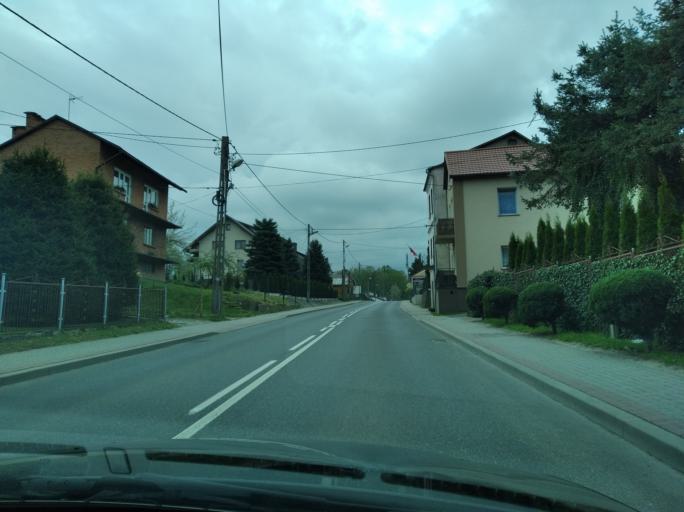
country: PL
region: Subcarpathian Voivodeship
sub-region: Powiat rzeszowski
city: Dynow
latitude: 49.8120
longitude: 22.2329
